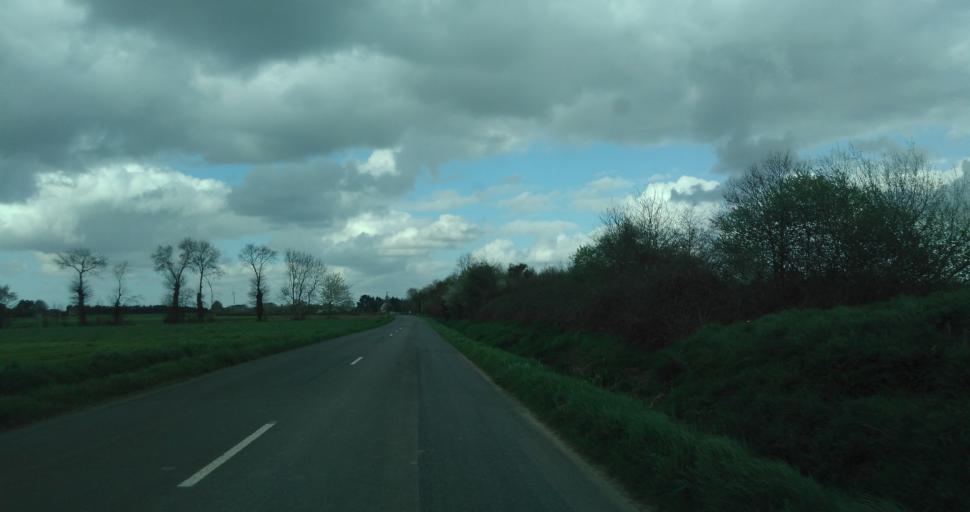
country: FR
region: Brittany
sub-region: Departement d'Ille-et-Vilaine
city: Chavagne
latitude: 48.0747
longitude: -1.7619
